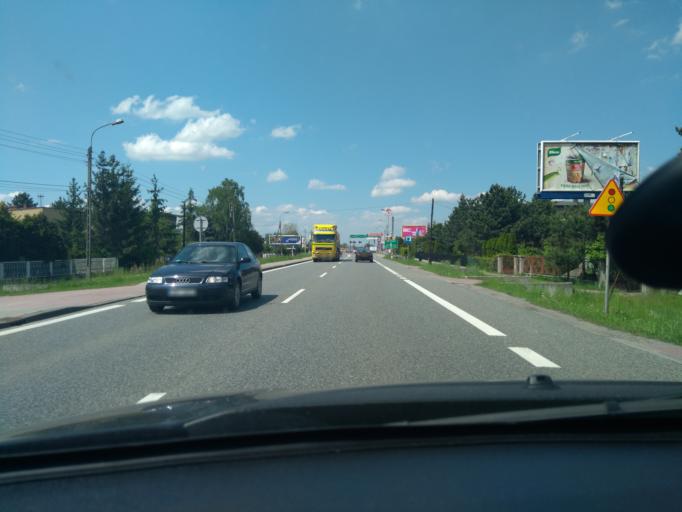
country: PL
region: Silesian Voivodeship
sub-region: Ruda Slaska
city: Ruda Slaska
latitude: 50.2190
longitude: 18.8308
